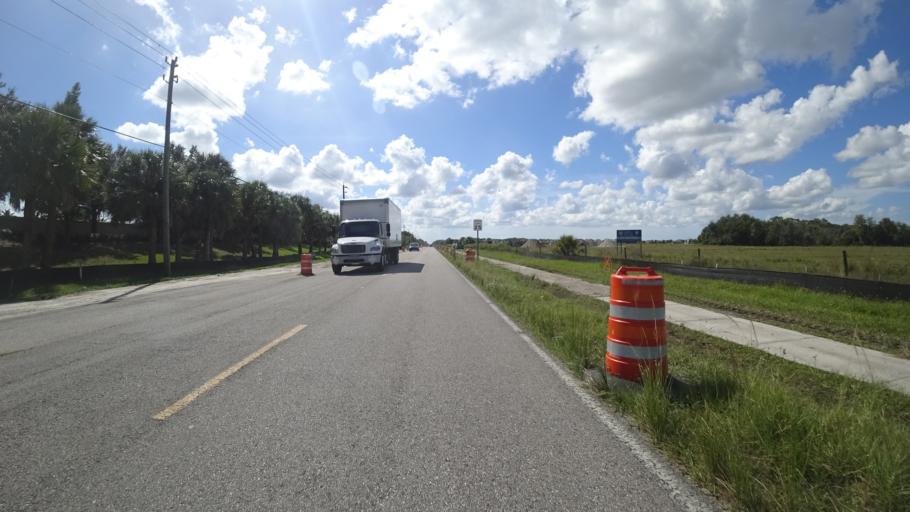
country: US
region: Florida
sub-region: Manatee County
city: Ellenton
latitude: 27.5051
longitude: -82.3749
